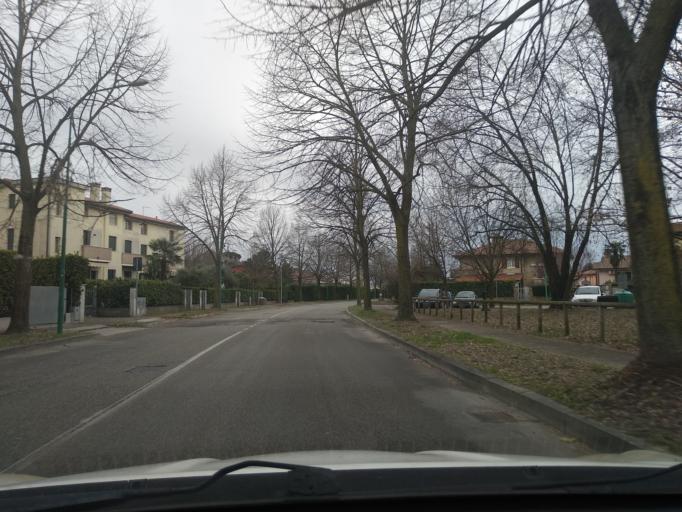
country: IT
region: Veneto
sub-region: Provincia di Padova
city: Selvazzano Dentro
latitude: 45.3873
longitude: 11.7850
